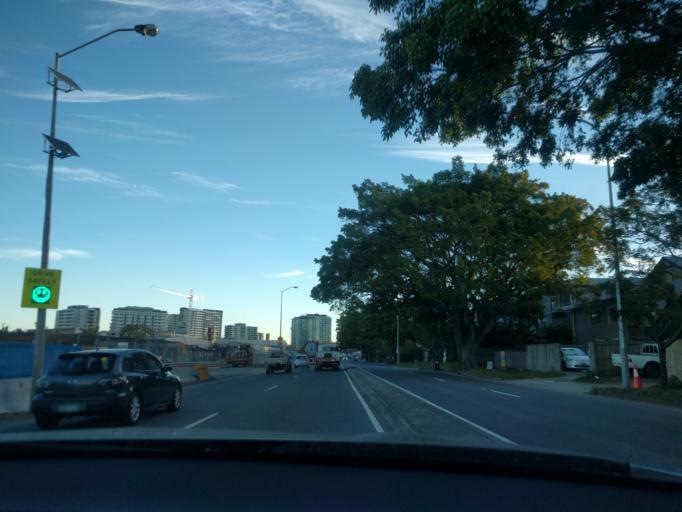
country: AU
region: Queensland
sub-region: Brisbane
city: Ascot
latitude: -27.4360
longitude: 153.0748
